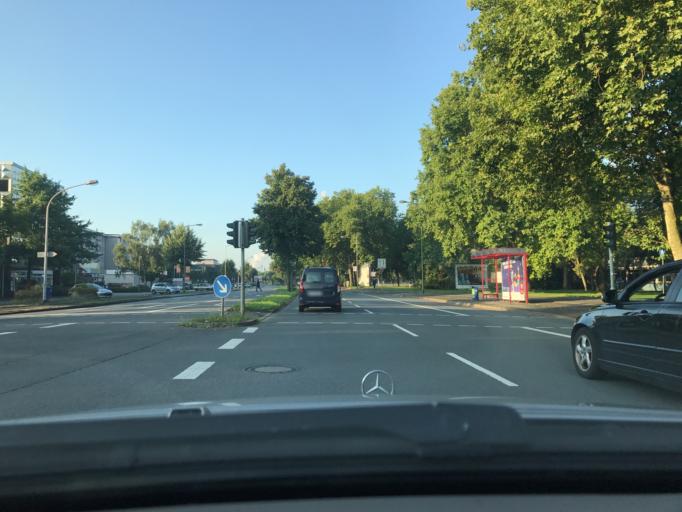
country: DE
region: North Rhine-Westphalia
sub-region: Regierungsbezirk Dusseldorf
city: Hochfeld
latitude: 51.4045
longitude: 6.7114
